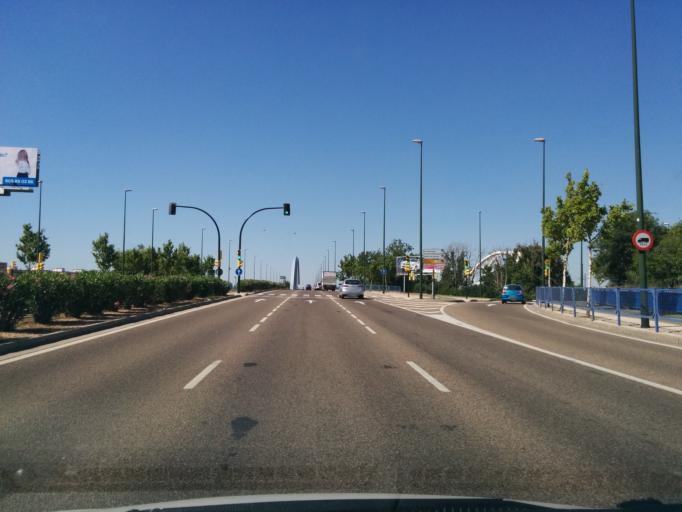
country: ES
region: Aragon
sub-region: Provincia de Zaragoza
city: Zaragoza
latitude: 41.6480
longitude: -0.8553
